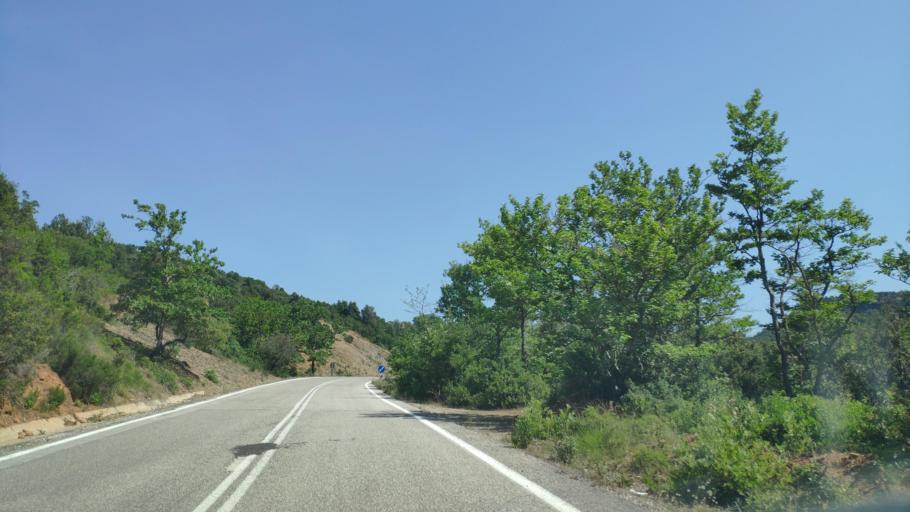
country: GR
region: West Greece
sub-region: Nomos Aitolias kai Akarnanias
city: Lepenou
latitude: 38.7831
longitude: 21.3341
